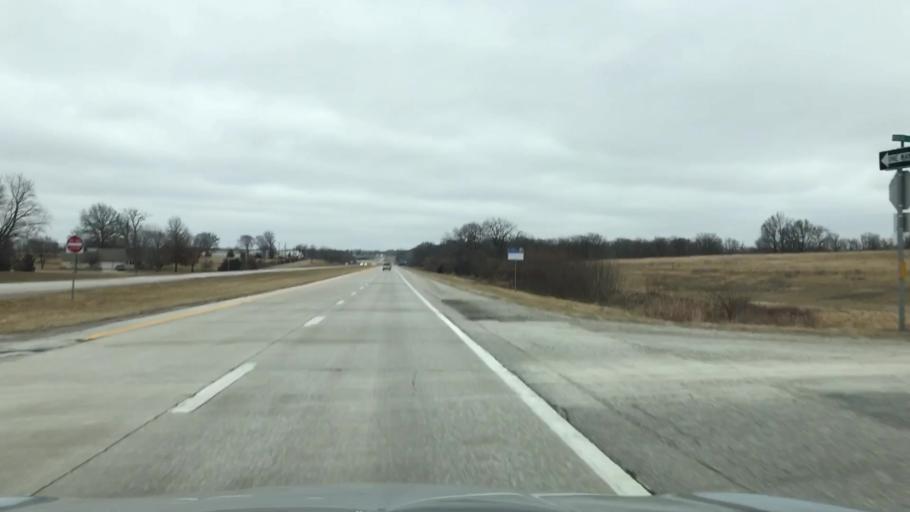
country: US
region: Missouri
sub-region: Linn County
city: Brookfield
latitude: 39.7783
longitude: -93.0989
